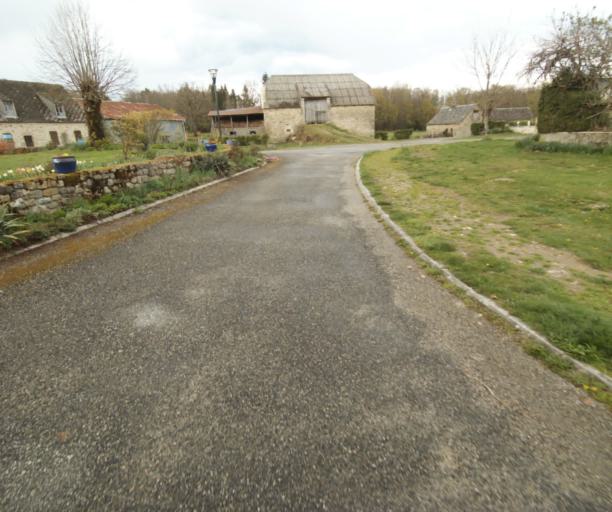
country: FR
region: Limousin
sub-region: Departement de la Correze
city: Saint-Privat
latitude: 45.2143
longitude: 2.0197
